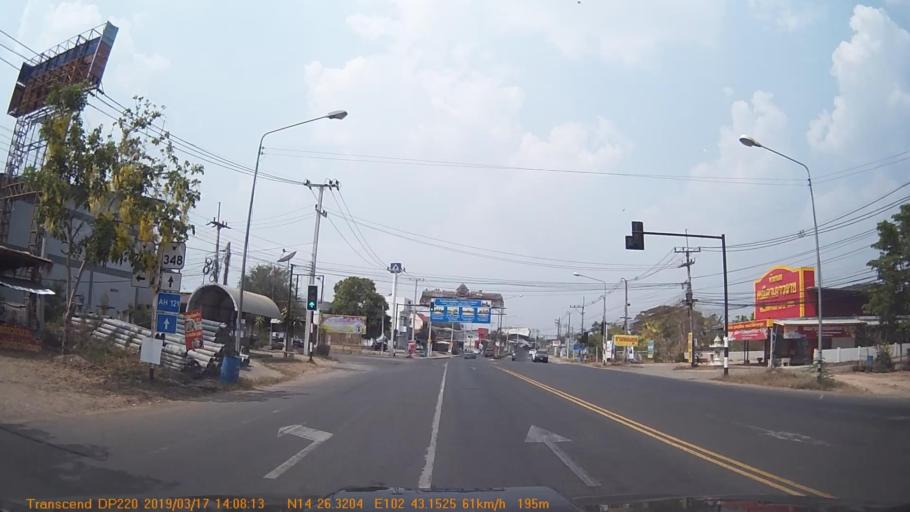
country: TH
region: Buriram
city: Pa Kham
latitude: 14.4389
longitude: 102.7192
